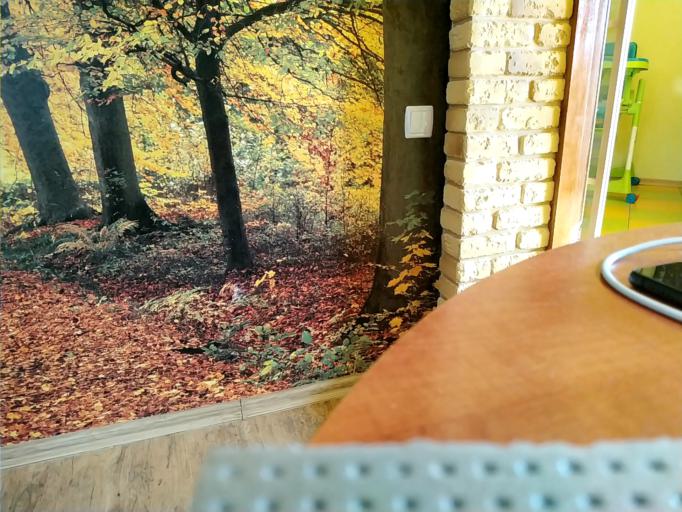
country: RU
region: Tverskaya
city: Kalashnikovo
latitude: 57.3492
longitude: 35.1941
